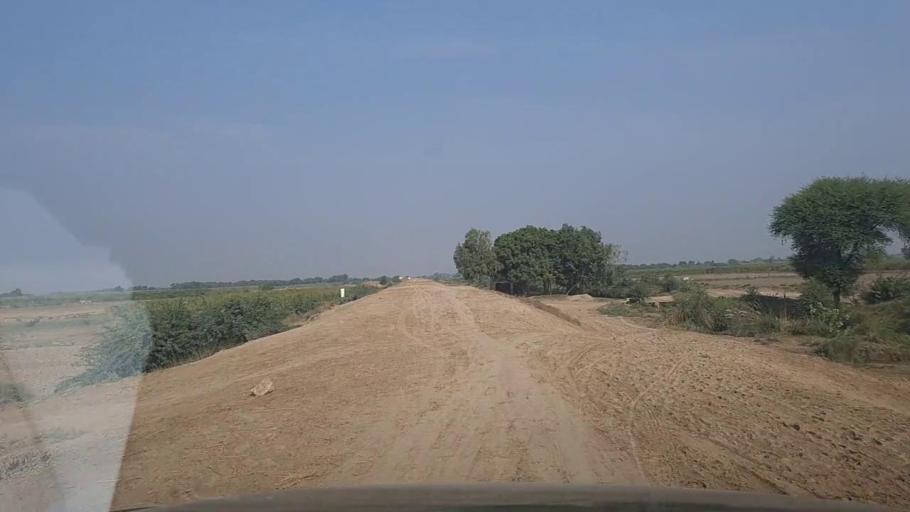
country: PK
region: Sindh
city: Bulri
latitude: 24.9968
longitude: 68.2904
